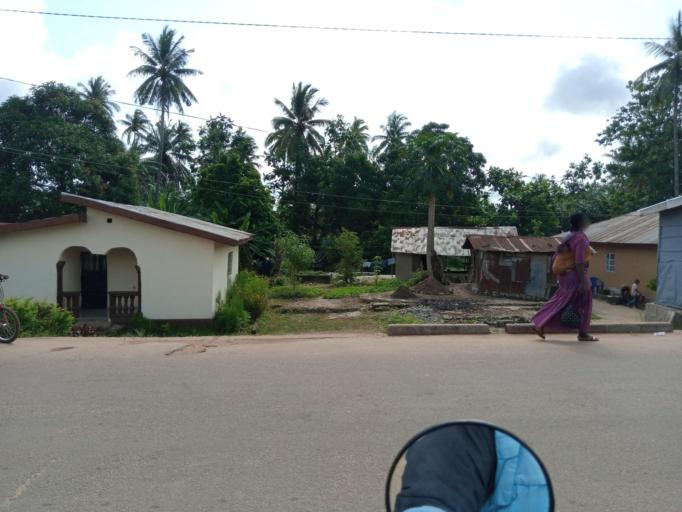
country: SL
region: Southern Province
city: Bo
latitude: 7.9729
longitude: -11.7378
